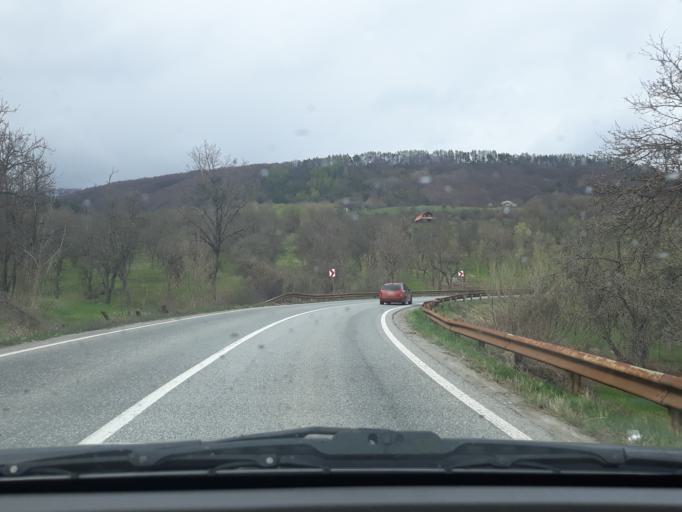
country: RO
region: Harghita
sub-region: Comuna Lupeni
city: Lupeni
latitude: 46.4073
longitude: 25.2126
